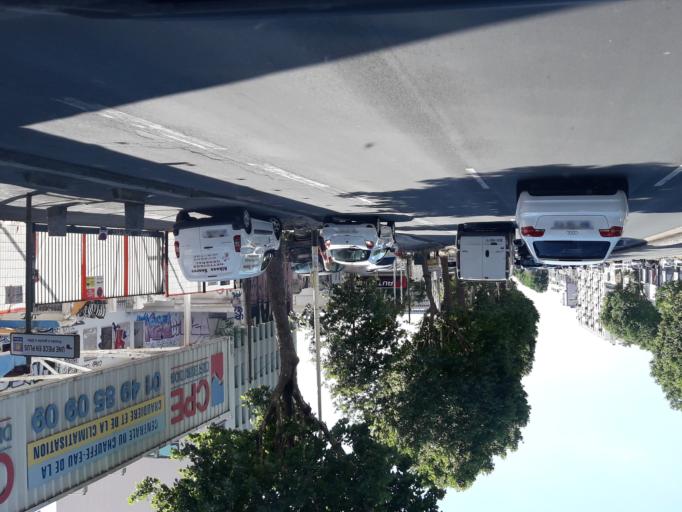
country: FR
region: Ile-de-France
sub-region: Departement du Val-de-Marne
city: Arcueil
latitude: 48.8087
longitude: 2.3263
